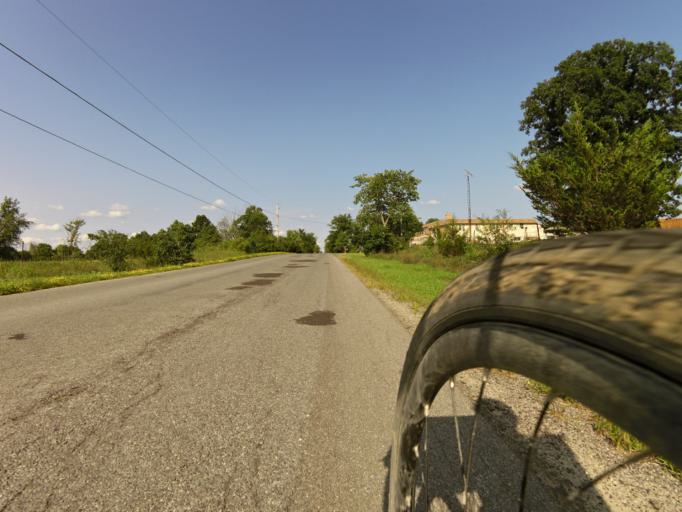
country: CA
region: Ontario
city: Kingston
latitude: 44.3382
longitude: -76.6630
